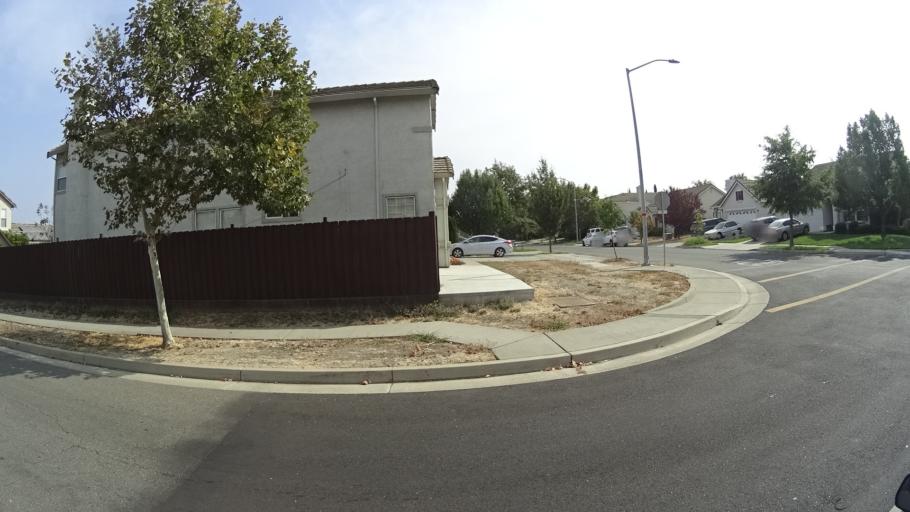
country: US
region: California
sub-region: Sacramento County
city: Laguna
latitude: 38.4472
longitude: -121.4101
